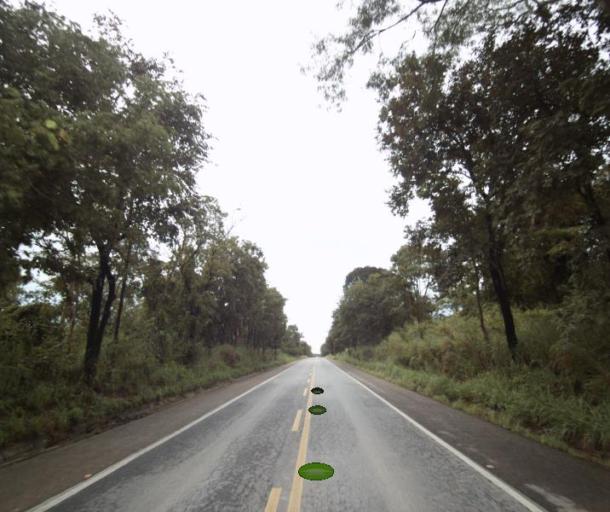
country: BR
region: Goias
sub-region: Porangatu
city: Porangatu
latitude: -13.6666
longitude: -49.0306
